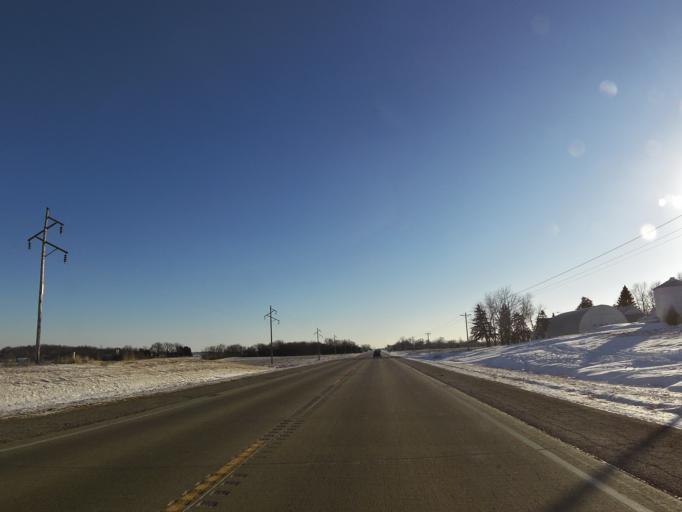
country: US
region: Minnesota
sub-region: Le Sueur County
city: New Prague
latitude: 44.5078
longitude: -93.5857
